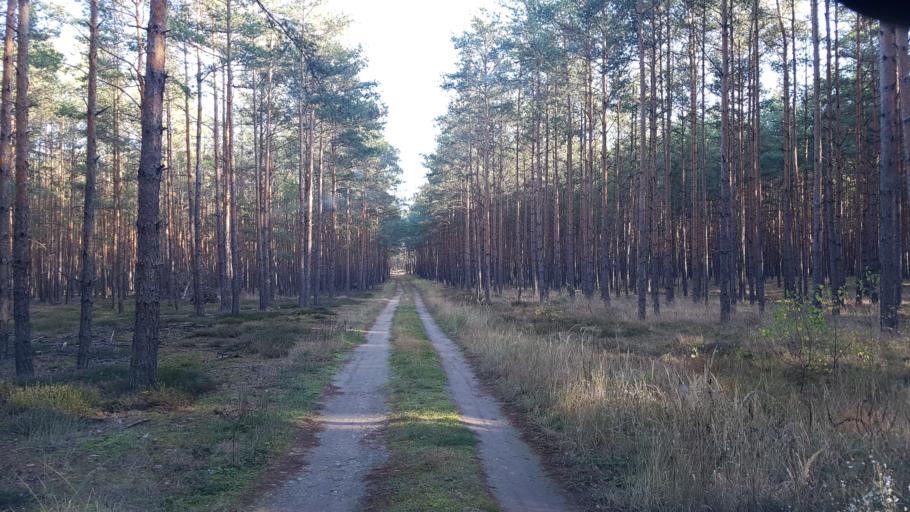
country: DE
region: Brandenburg
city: Sonnewalde
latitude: 51.6457
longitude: 13.6437
